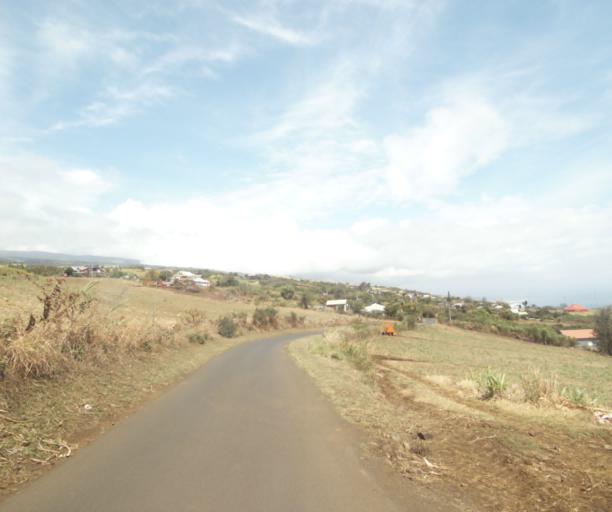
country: RE
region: Reunion
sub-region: Reunion
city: Trois-Bassins
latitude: -21.0940
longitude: 55.2760
